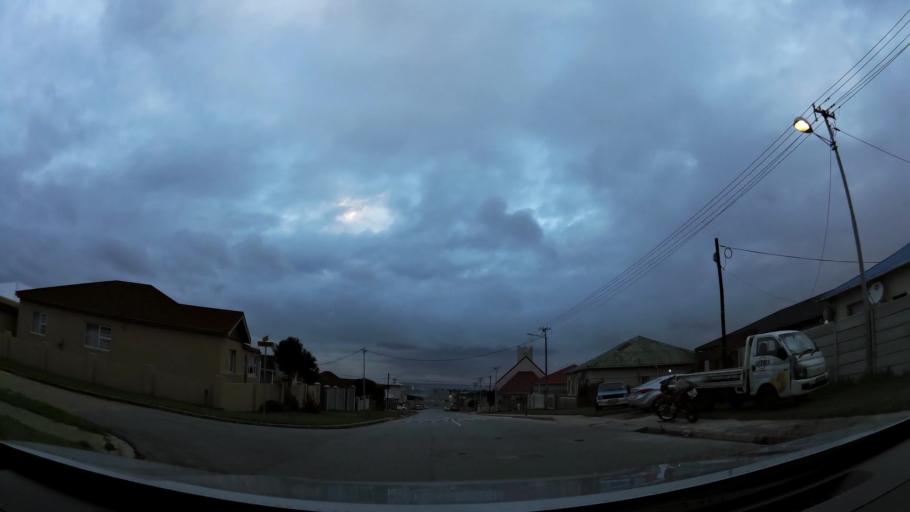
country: ZA
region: Eastern Cape
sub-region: Nelson Mandela Bay Metropolitan Municipality
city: Port Elizabeth
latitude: -33.9303
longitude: 25.5987
